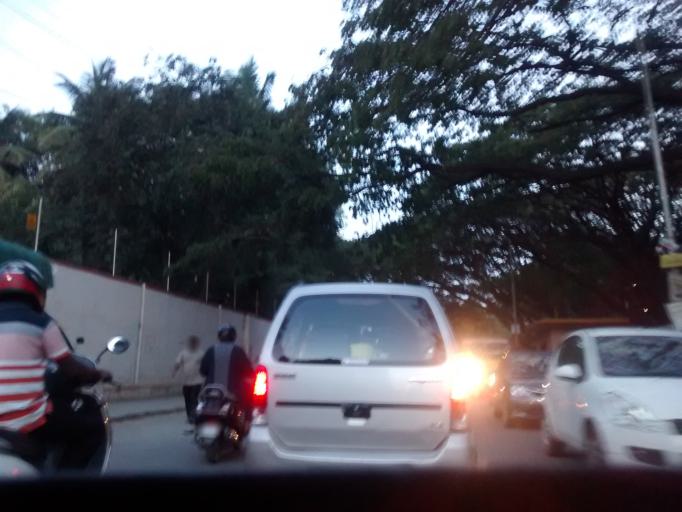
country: IN
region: Karnataka
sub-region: Bangalore Urban
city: Bangalore
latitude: 12.9715
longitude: 77.6598
